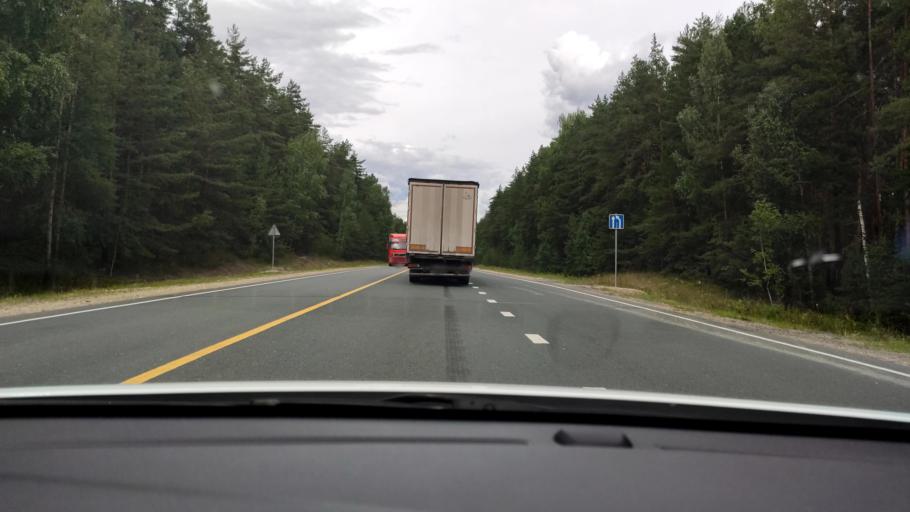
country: RU
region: Mariy-El
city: Pomary
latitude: 56.0222
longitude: 48.3814
